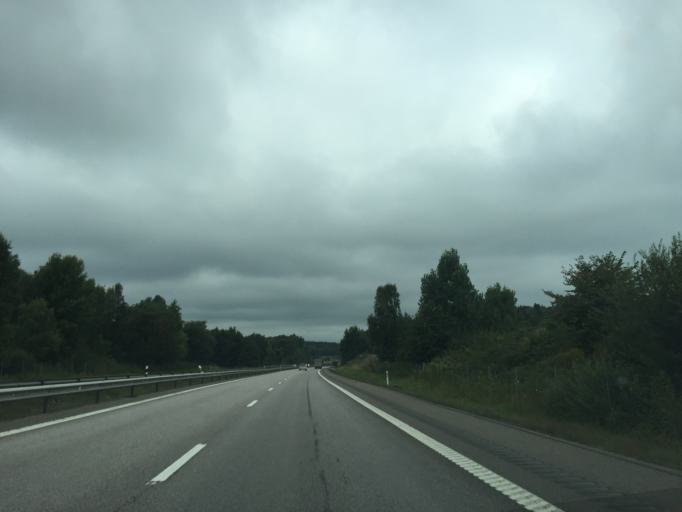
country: SE
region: Halland
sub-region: Kungsbacka Kommun
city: Fjaeras kyrkby
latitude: 57.4093
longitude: 12.1744
